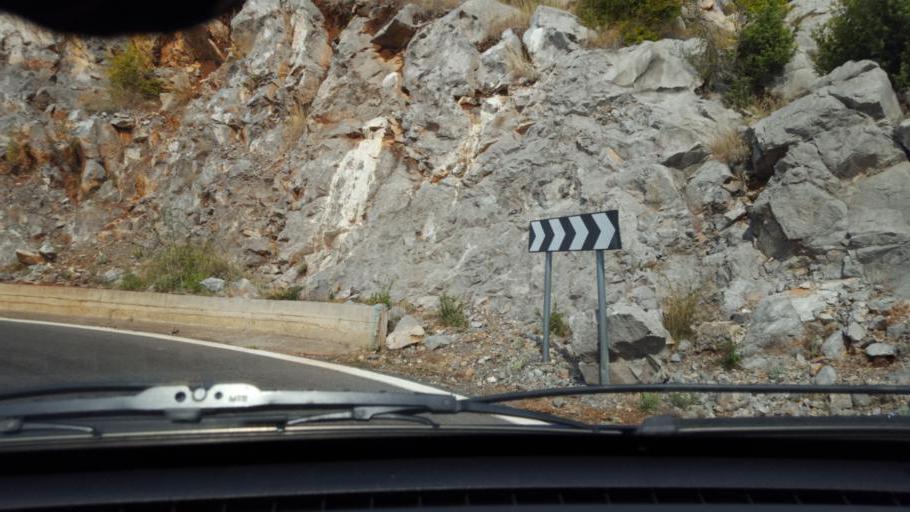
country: AL
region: Shkoder
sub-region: Rrethi i Malesia e Madhe
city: Hot
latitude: 42.3736
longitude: 19.4549
